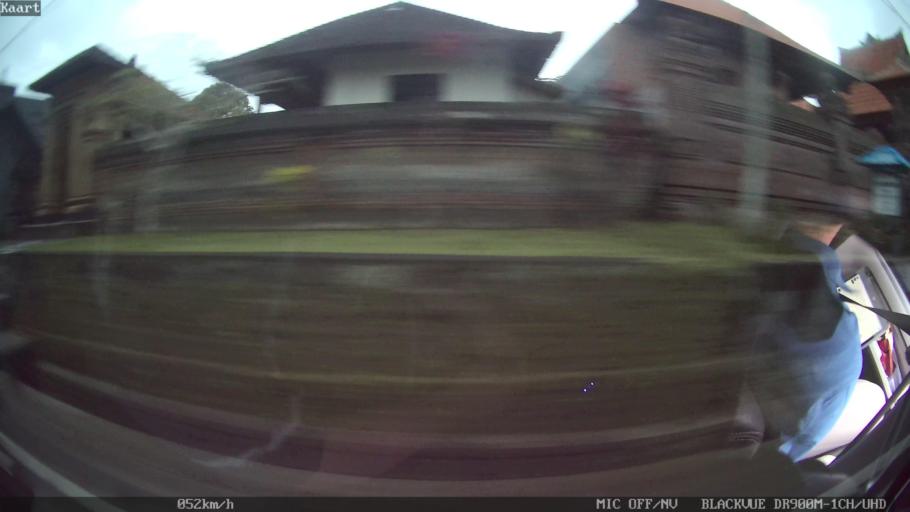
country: ID
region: Bali
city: Bayad
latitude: -8.4468
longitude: 115.2421
